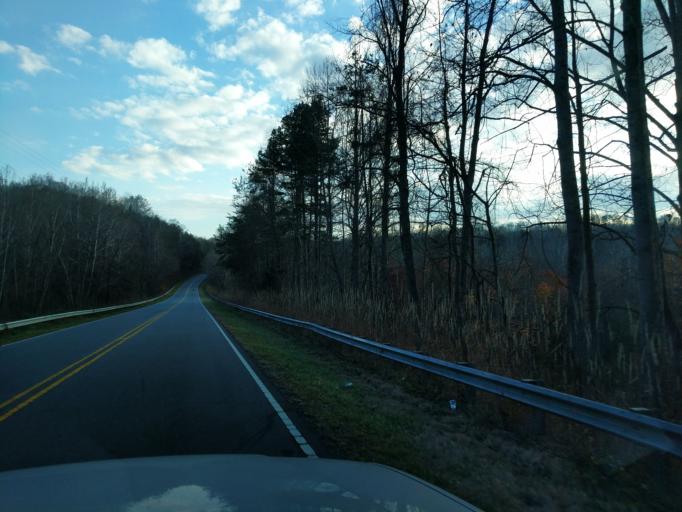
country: US
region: North Carolina
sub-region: Rutherford County
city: Rutherfordton
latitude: 35.4626
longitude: -81.9797
